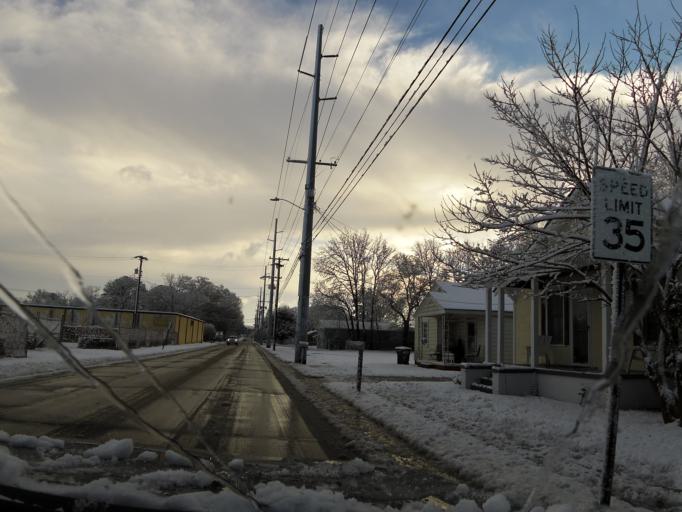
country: US
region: North Carolina
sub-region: Nash County
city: Rocky Mount
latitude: 35.9267
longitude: -77.8092
